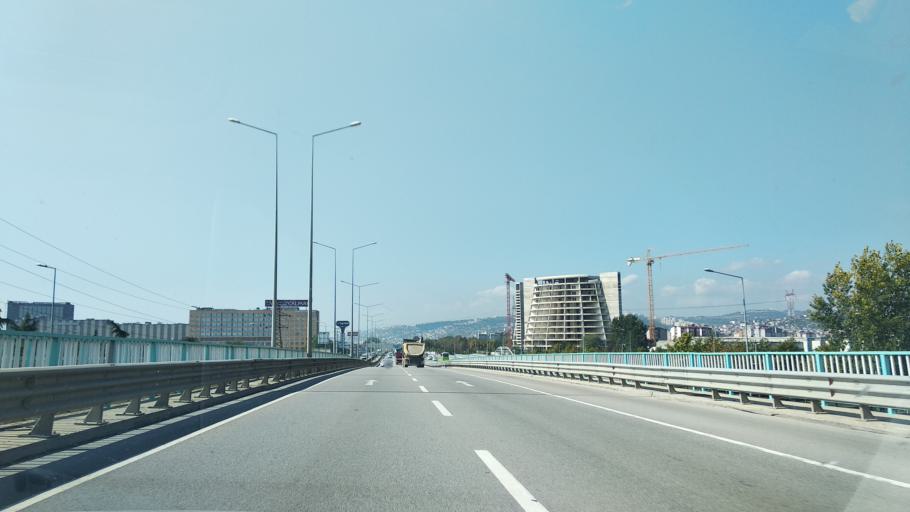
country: TR
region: Kocaeli
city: Kosekoy
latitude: 40.7586
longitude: 29.9876
